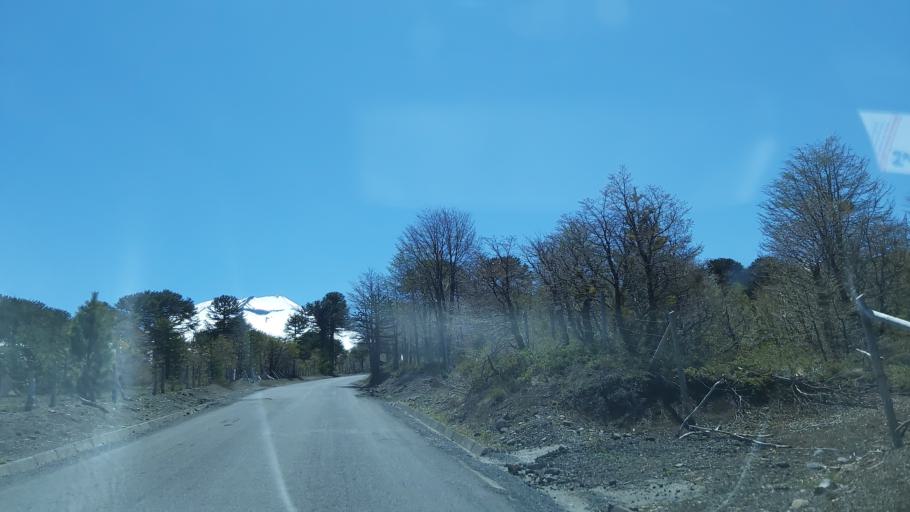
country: CL
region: Araucania
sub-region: Provincia de Cautin
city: Vilcun
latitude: -38.4337
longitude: -71.5363
